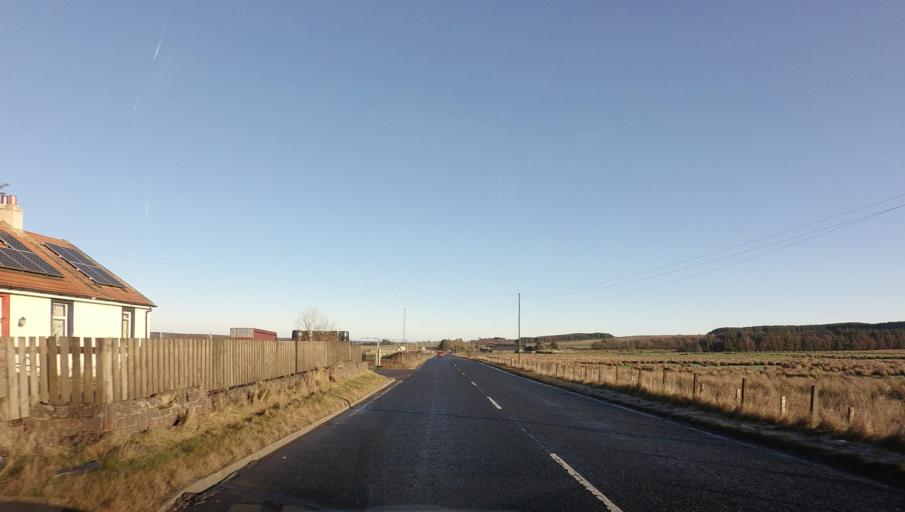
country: GB
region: Scotland
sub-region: West Lothian
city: Fauldhouse
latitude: 55.8200
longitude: -3.6903
